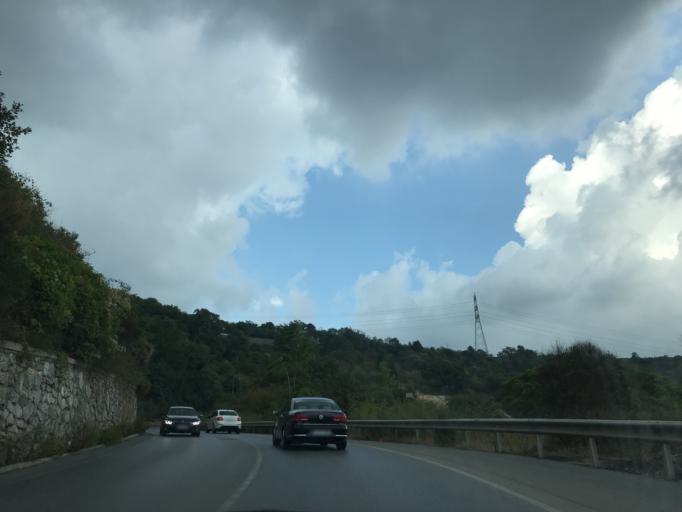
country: TR
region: Istanbul
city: Arikoey
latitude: 41.1822
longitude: 29.0452
